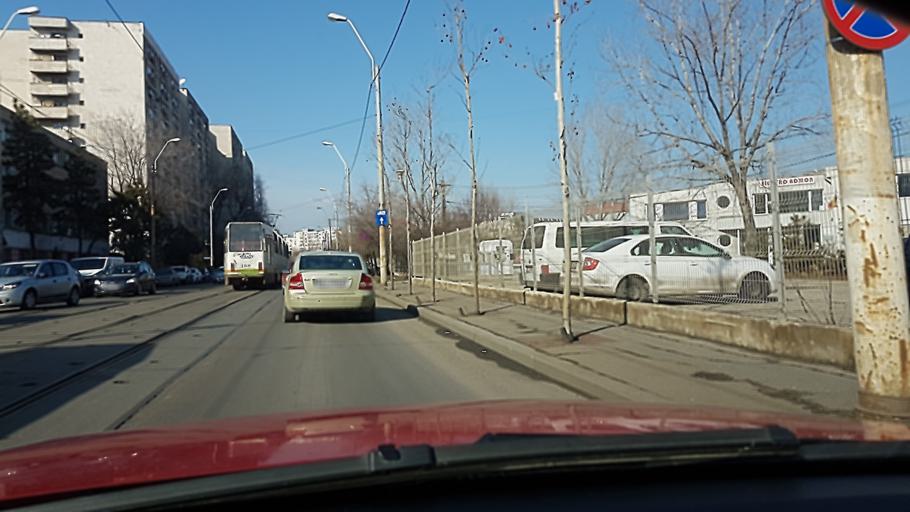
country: RO
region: Ilfov
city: Dobroesti
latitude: 44.4304
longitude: 26.1734
